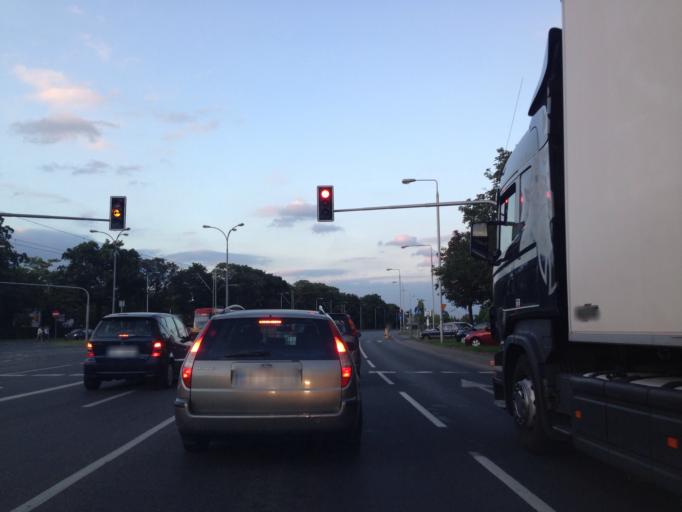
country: PL
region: Masovian Voivodeship
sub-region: Warszawa
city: Zoliborz
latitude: 52.2562
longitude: 20.9869
